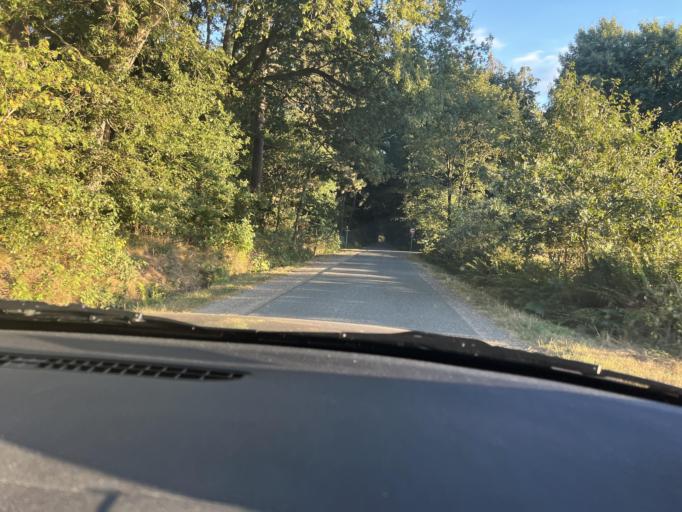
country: DE
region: Schleswig-Holstein
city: Weddingstedt
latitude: 54.2234
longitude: 9.1039
